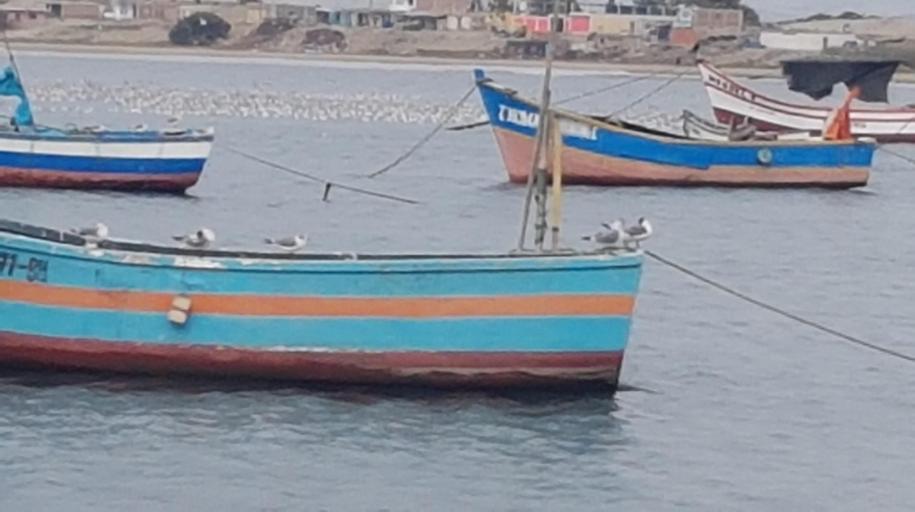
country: PE
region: Ancash
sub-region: Provincia de Santa
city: Puerto Santa
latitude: -8.9902
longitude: -78.6525
